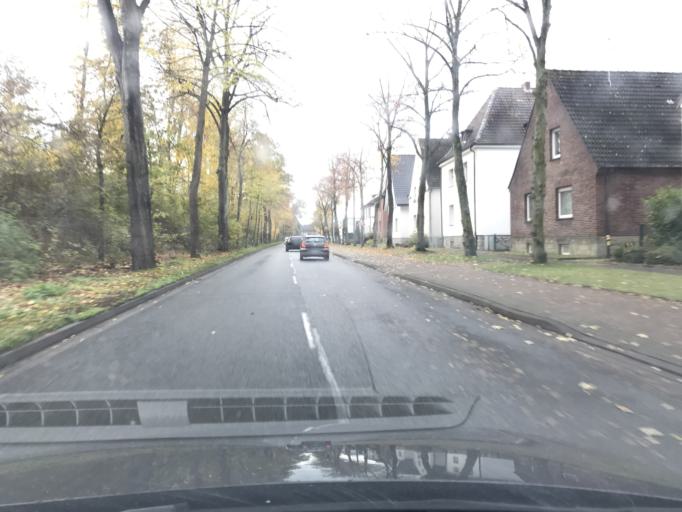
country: DE
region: North Rhine-Westphalia
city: Oelde
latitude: 51.8314
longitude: 8.1550
